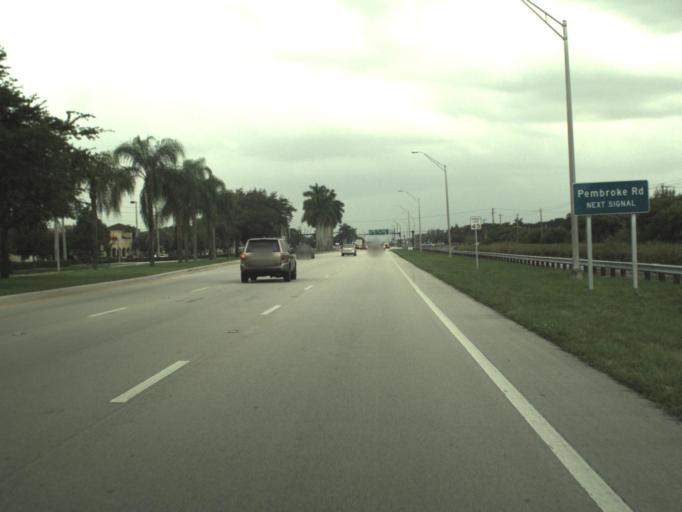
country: US
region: Florida
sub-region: Miami-Dade County
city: Country Club
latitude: 25.9974
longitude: -80.3118
